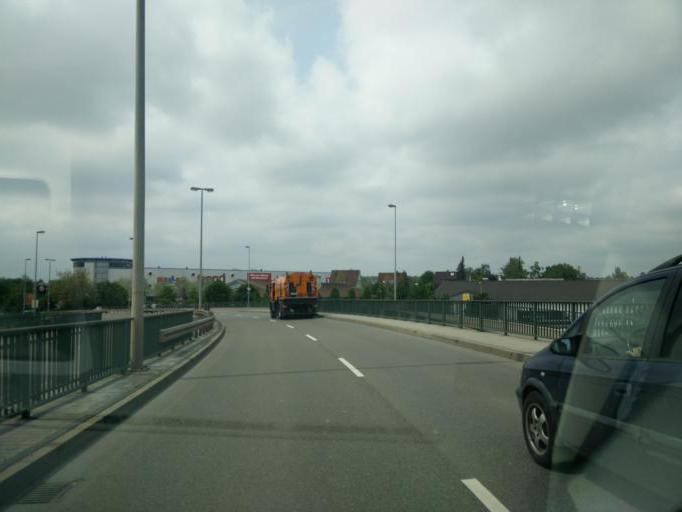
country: DE
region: Baden-Wuerttemberg
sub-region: Tuebingen Region
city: Reutlingen
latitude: 48.5016
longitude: 9.2101
